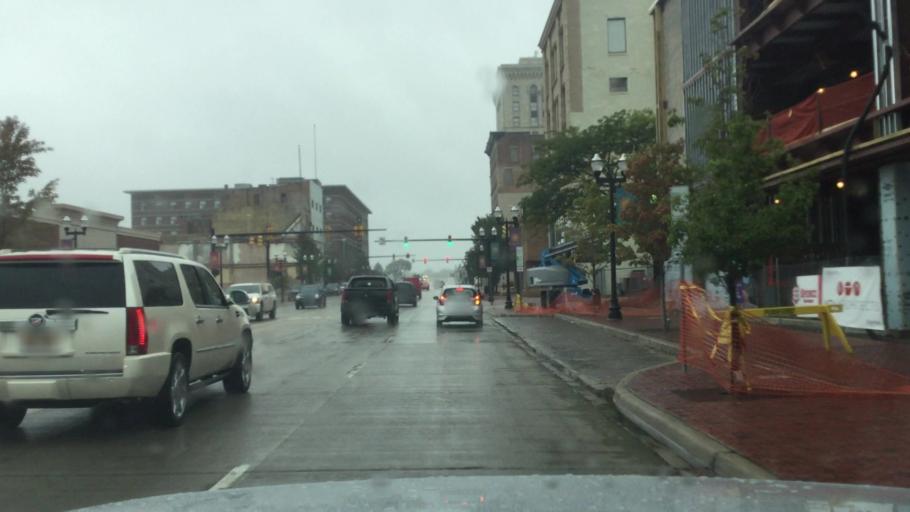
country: US
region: Michigan
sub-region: Saginaw County
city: Saginaw
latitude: 43.4329
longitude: -83.9368
